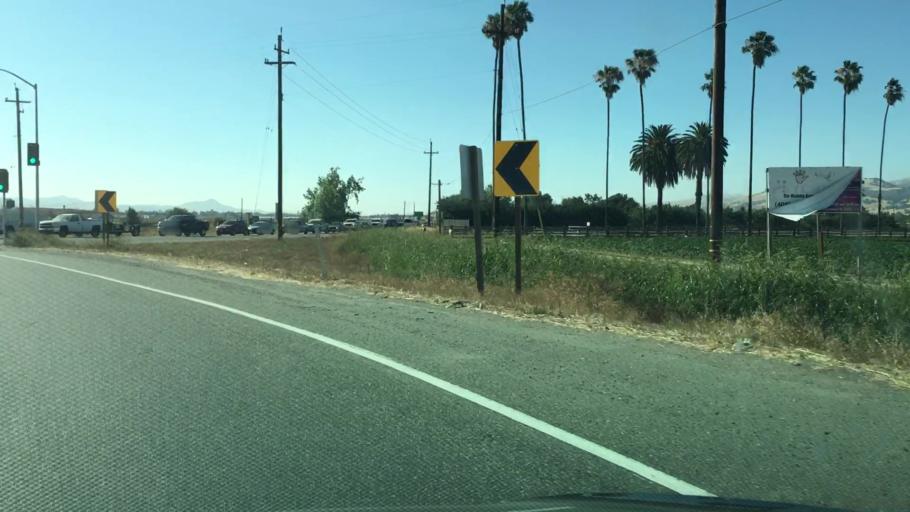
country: US
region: California
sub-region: Santa Clara County
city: Gilroy
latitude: 37.0098
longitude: -121.5152
